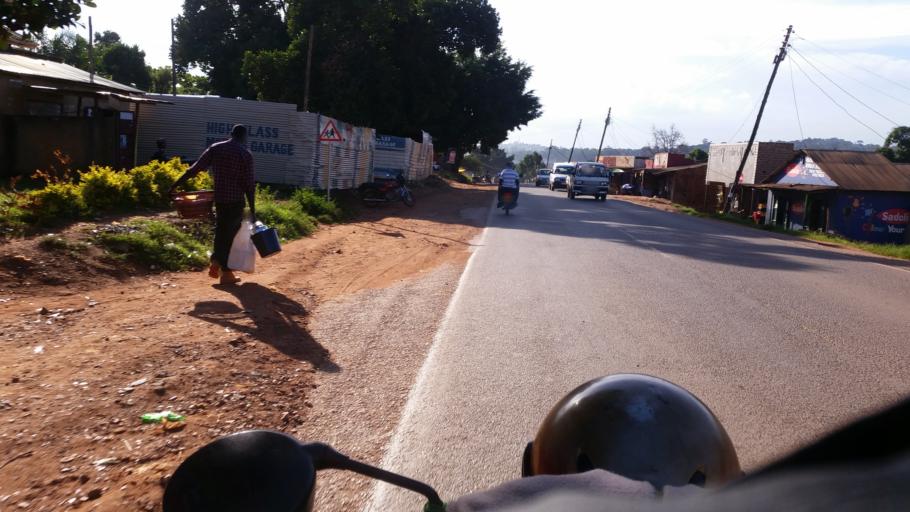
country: UG
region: Central Region
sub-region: Wakiso District
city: Kireka
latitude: 0.3295
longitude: 32.6376
